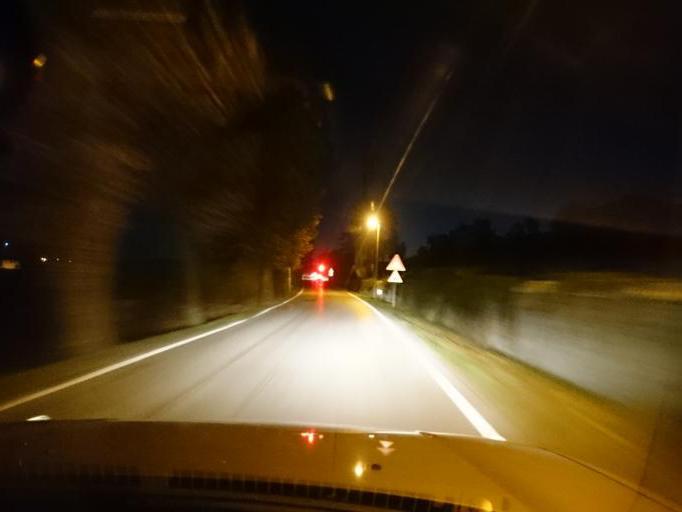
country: IT
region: Veneto
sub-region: Provincia di Padova
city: Baone
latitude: 45.2370
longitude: 11.6756
